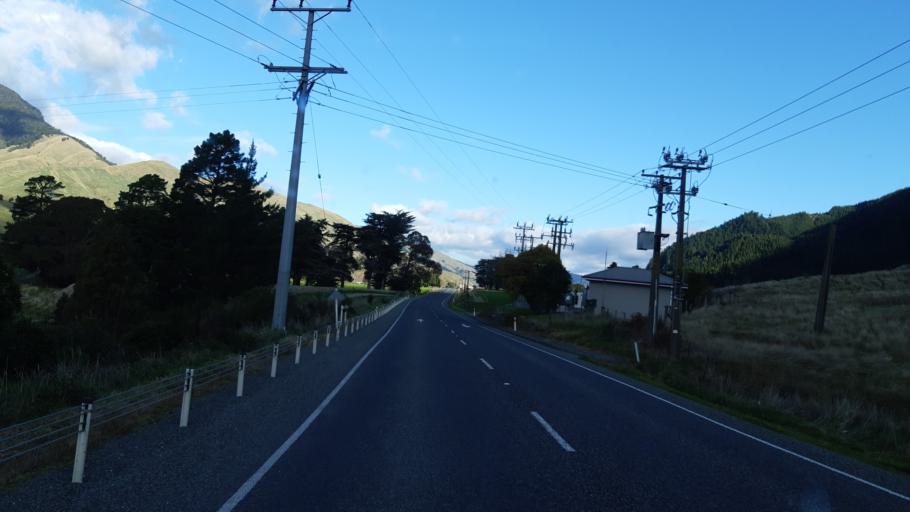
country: NZ
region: Marlborough
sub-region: Marlborough District
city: Picton
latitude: -41.2955
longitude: 173.7700
